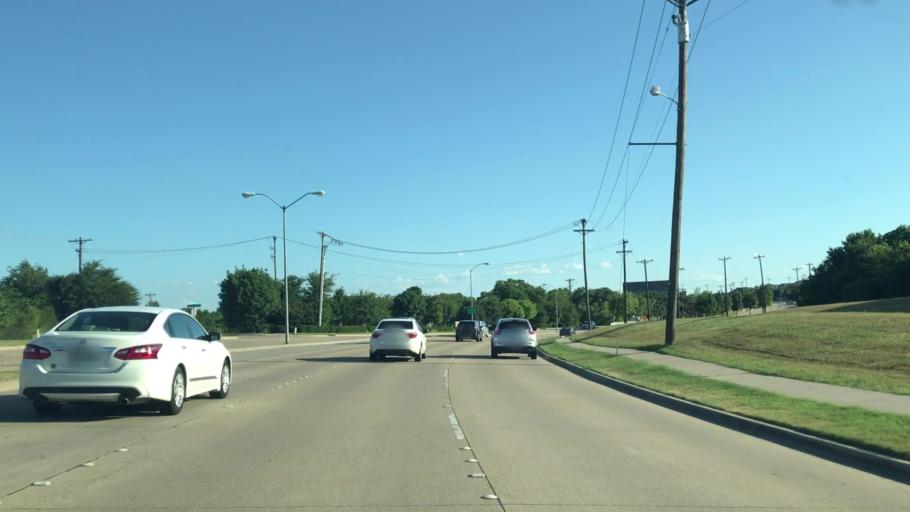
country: US
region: Texas
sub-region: Collin County
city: Allen
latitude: 33.0915
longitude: -96.7337
